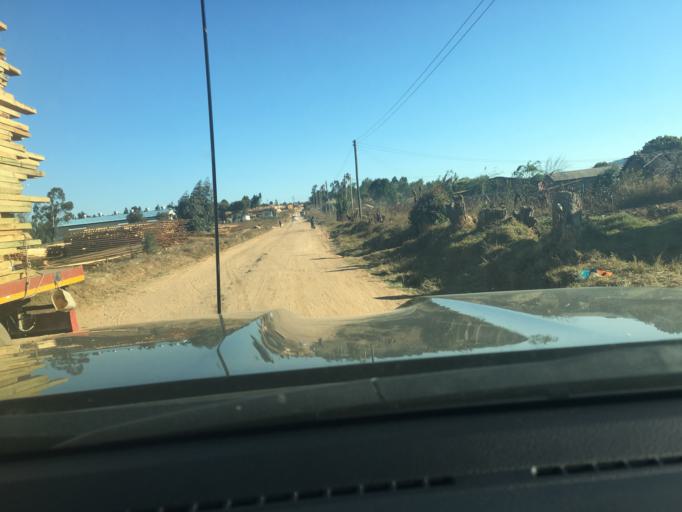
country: TZ
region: Iringa
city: Makungu
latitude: -8.4120
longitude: 35.4205
